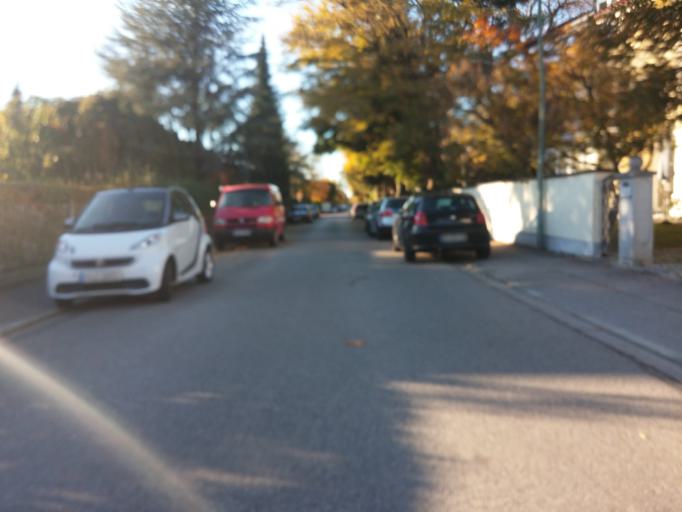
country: DE
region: Bavaria
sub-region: Upper Bavaria
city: Haar
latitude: 48.1068
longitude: 11.7109
